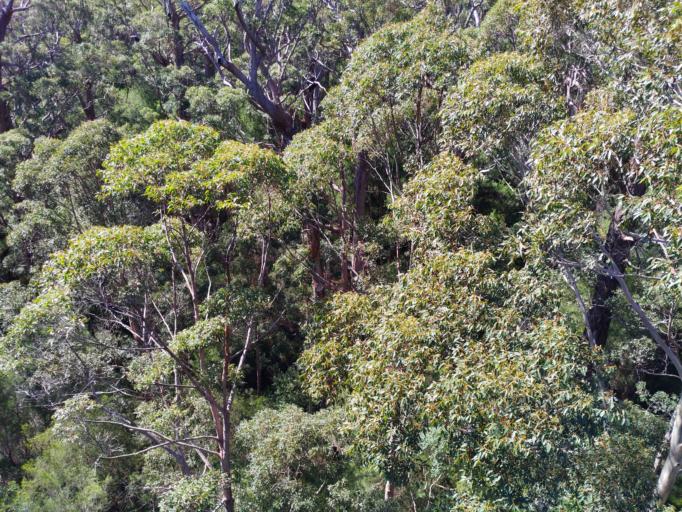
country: AU
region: Western Australia
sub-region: Denmark
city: Denmark
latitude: -34.9763
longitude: 116.8950
